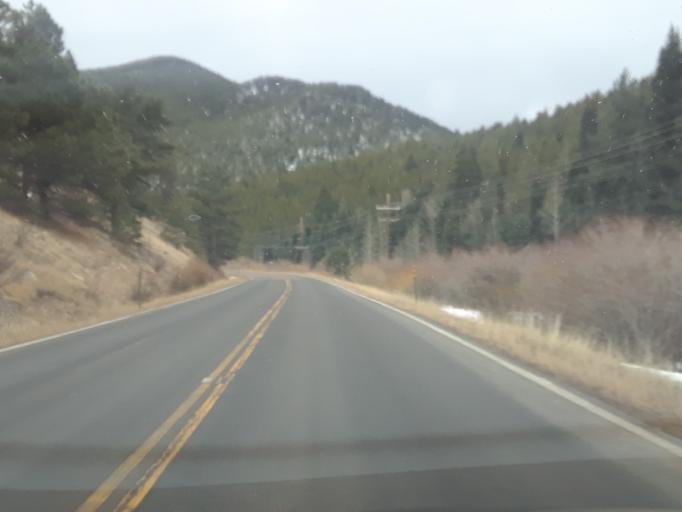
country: US
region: Colorado
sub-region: Boulder County
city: Coal Creek
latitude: 39.8302
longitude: -105.4174
